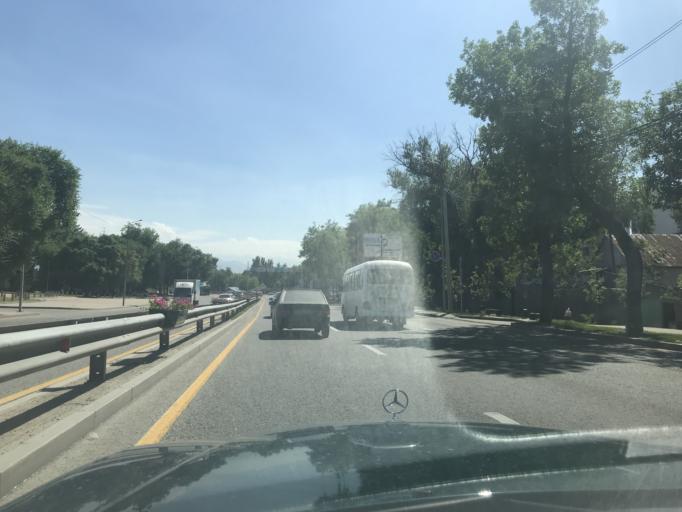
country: KZ
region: Almaty Qalasy
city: Almaty
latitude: 43.2890
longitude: 76.9893
